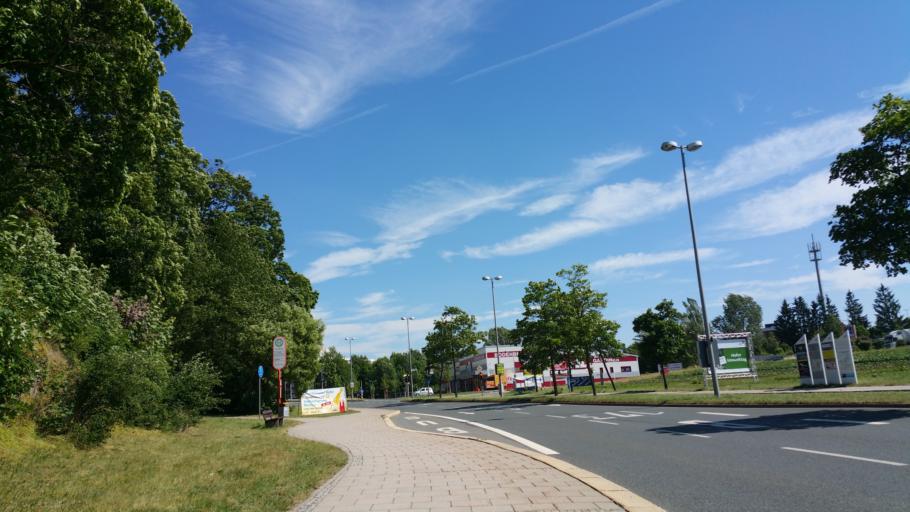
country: DE
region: Bavaria
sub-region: Upper Franconia
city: Hof
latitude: 50.3250
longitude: 11.8931
